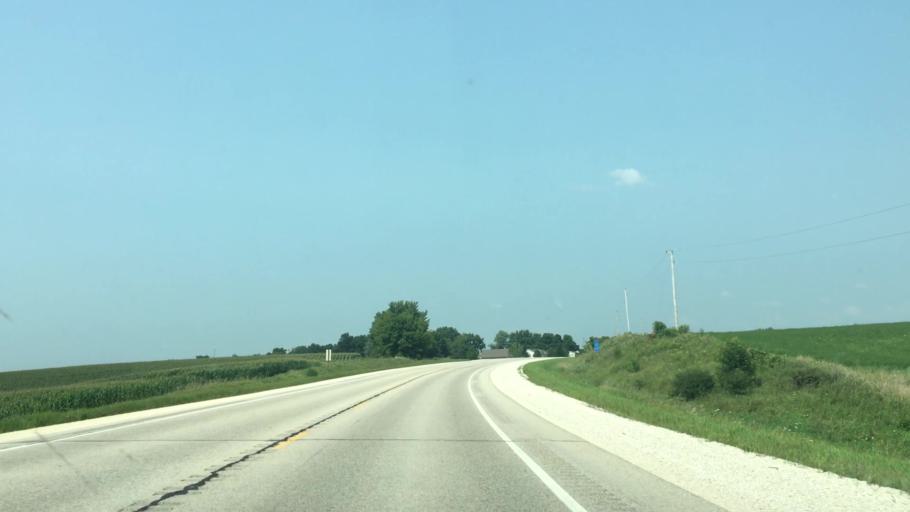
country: US
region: Iowa
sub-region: Winneshiek County
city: Decorah
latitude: 43.2597
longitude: -91.8381
